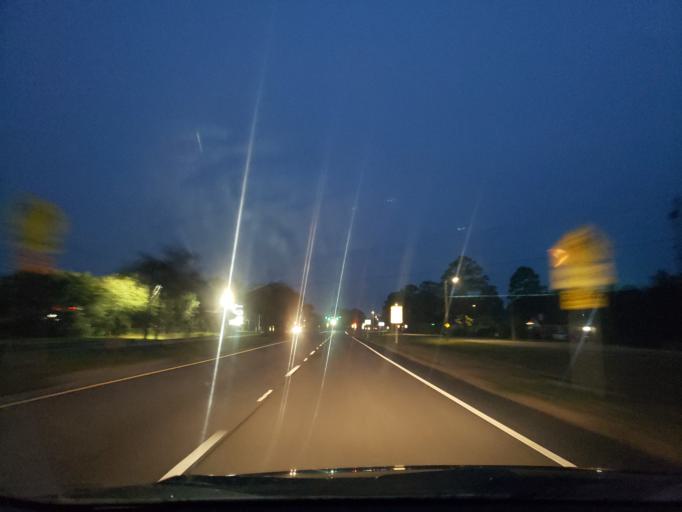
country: US
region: Georgia
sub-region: Chatham County
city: Whitemarsh Island
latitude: 32.0436
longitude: -81.0081
